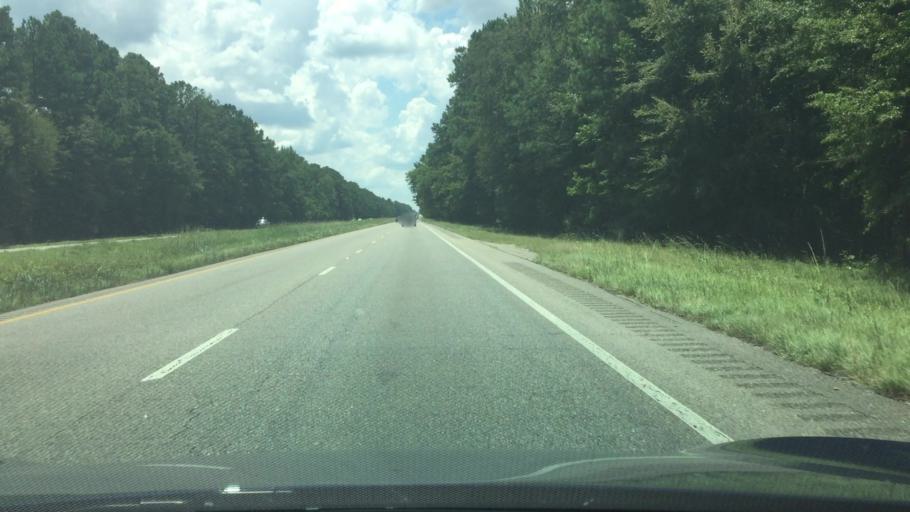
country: US
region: Alabama
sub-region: Montgomery County
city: Pike Road
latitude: 32.1025
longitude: -86.0656
